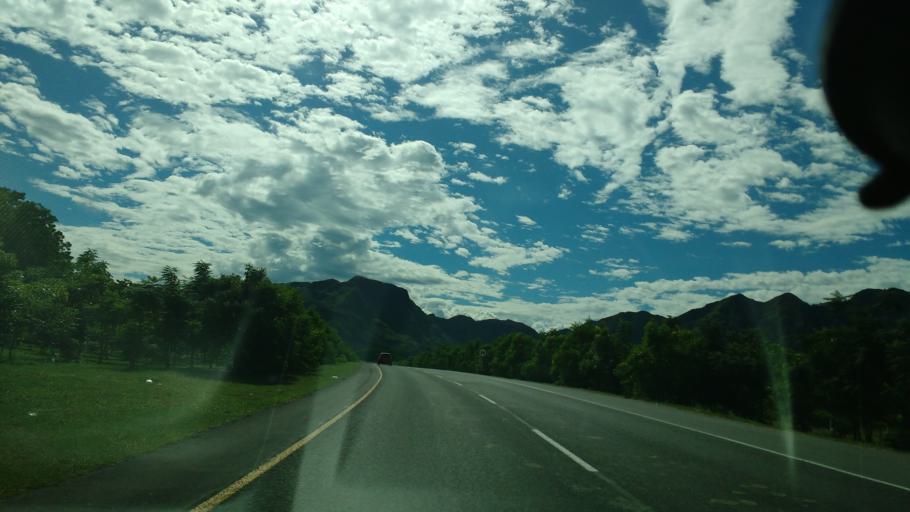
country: CO
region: Tolima
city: Valle de San Juan
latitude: 4.2723
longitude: -75.0004
